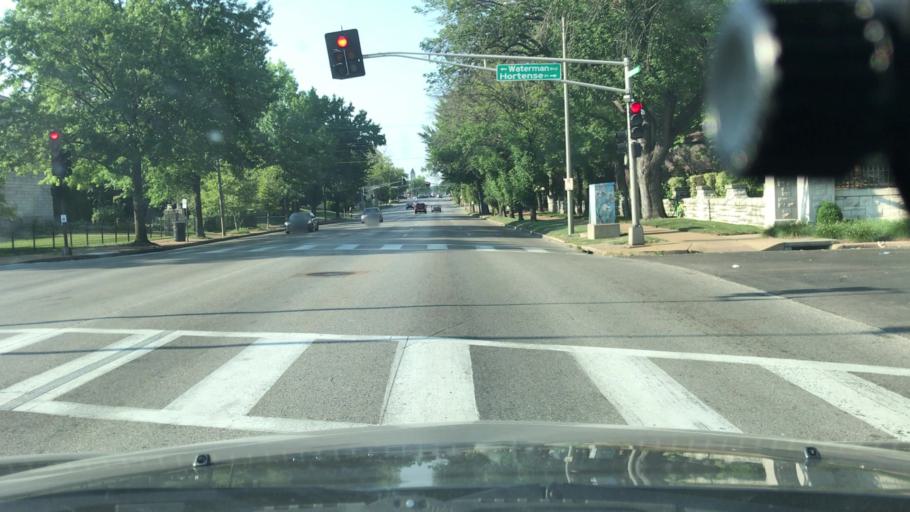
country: US
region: Missouri
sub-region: Saint Louis County
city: Hillsdale
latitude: 38.6480
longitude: -90.2641
